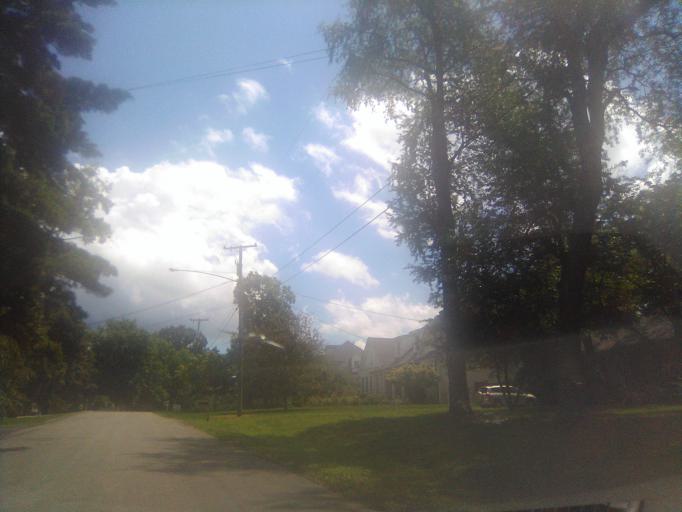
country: US
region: Tennessee
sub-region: Davidson County
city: Belle Meade
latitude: 36.1087
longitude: -86.8407
